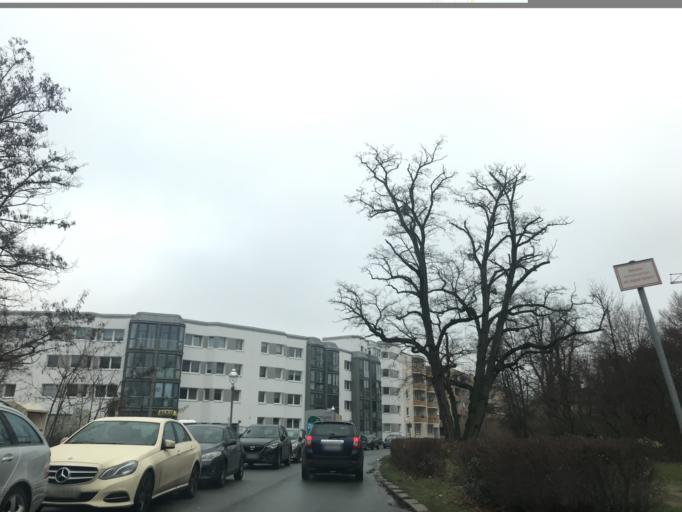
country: DE
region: Berlin
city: Hakenfelde
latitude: 52.5501
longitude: 13.2104
